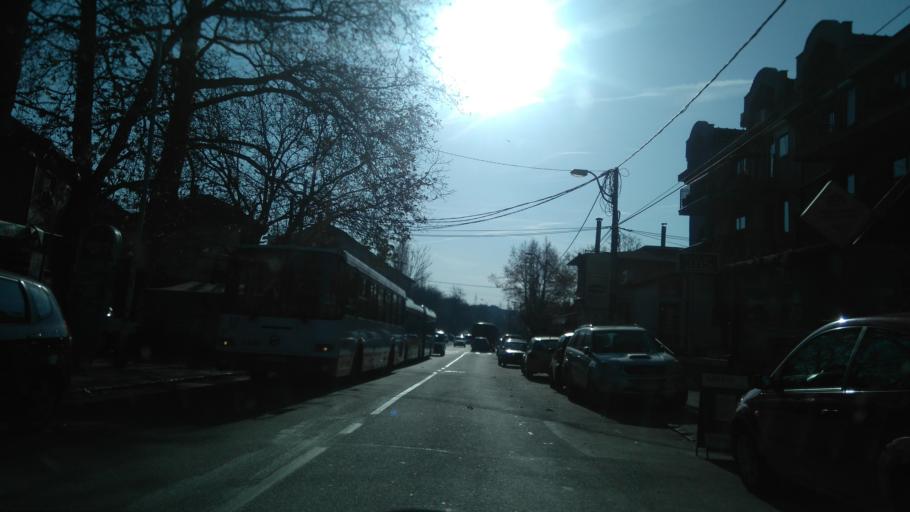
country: RS
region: Central Serbia
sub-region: Belgrade
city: Cukarica
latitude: 44.7556
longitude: 20.4043
